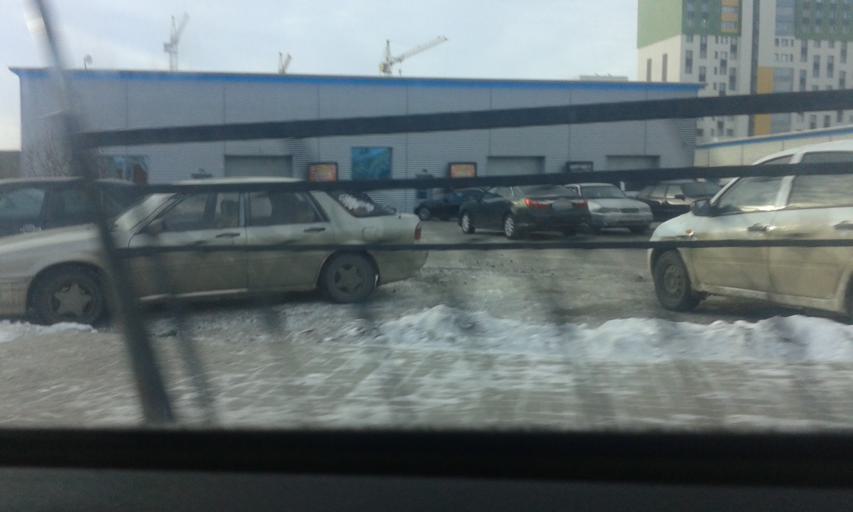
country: KZ
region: Astana Qalasy
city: Astana
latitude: 51.1455
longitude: 71.4602
